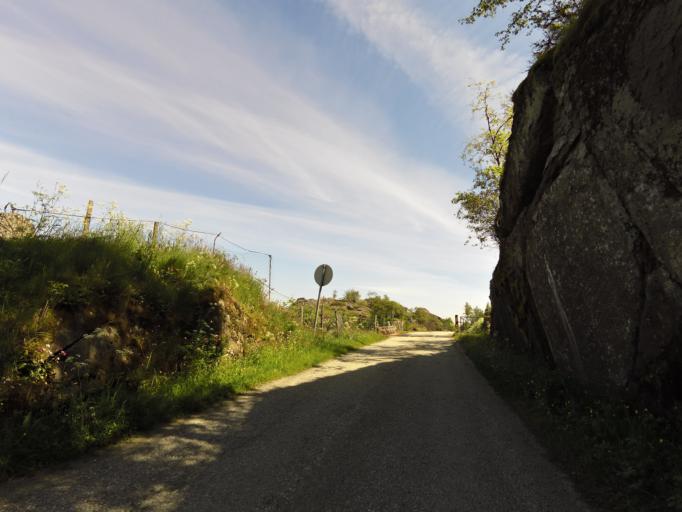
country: NO
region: Rogaland
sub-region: Sokndal
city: Hauge i Dalane
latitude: 58.3570
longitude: 6.1544
